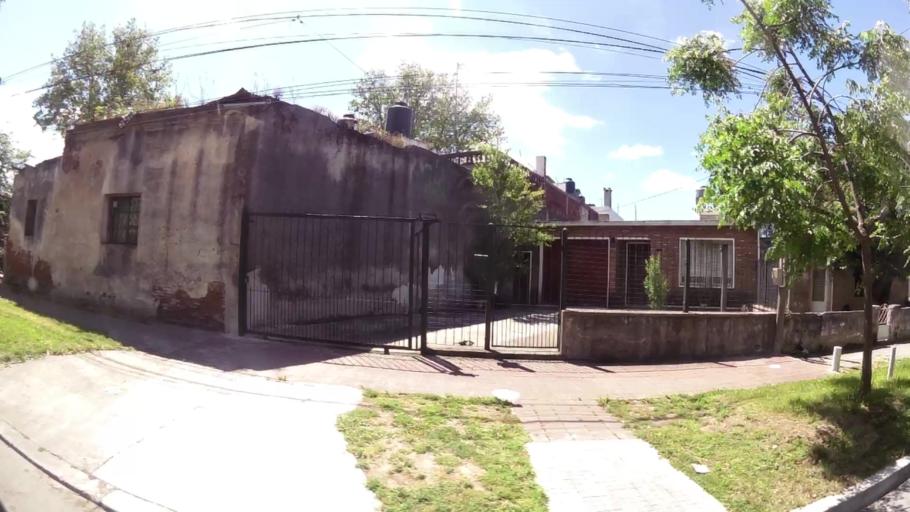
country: UY
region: Montevideo
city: Montevideo
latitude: -34.8590
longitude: -56.1348
